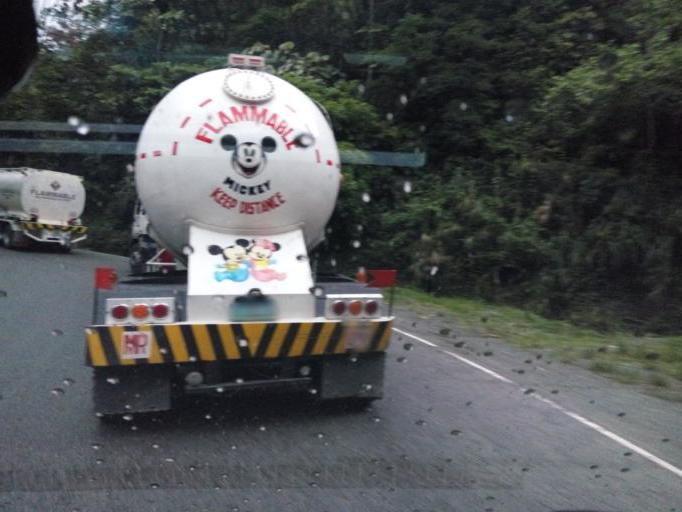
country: PH
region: Cagayan Valley
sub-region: Province of Nueva Vizcaya
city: Santa Fe
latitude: 16.1172
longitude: 120.9291
